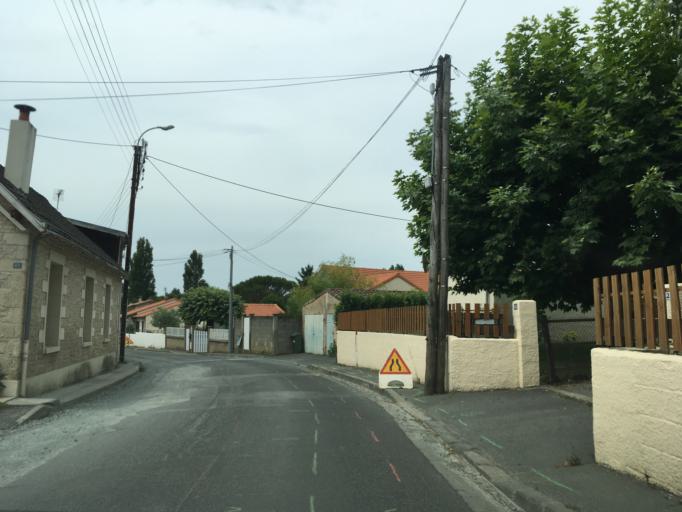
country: FR
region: Poitou-Charentes
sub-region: Departement des Deux-Sevres
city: Bessines
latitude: 46.3269
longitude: -0.5135
